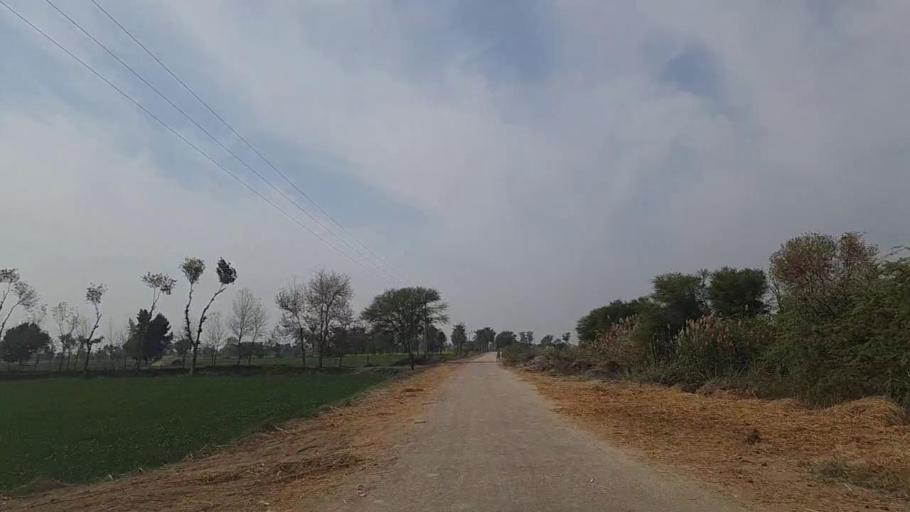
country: PK
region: Sindh
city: Daur
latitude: 26.4514
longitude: 68.4283
